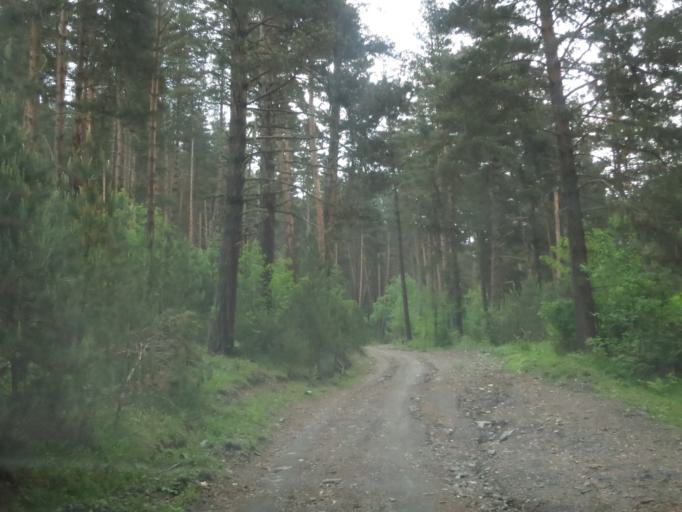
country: RU
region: Chechnya
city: Itum-Kali
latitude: 42.3598
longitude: 45.6545
